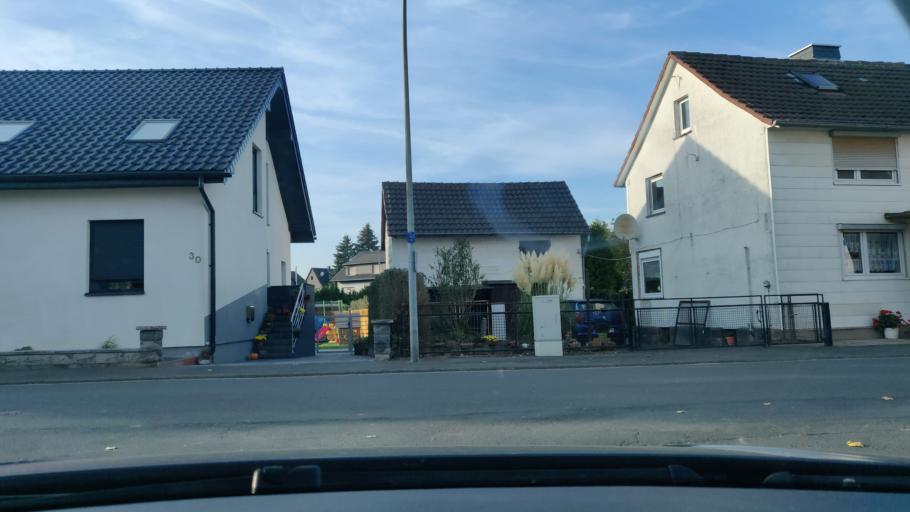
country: DE
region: Hesse
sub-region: Regierungsbezirk Kassel
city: Wabern
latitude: 51.0984
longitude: 9.3452
